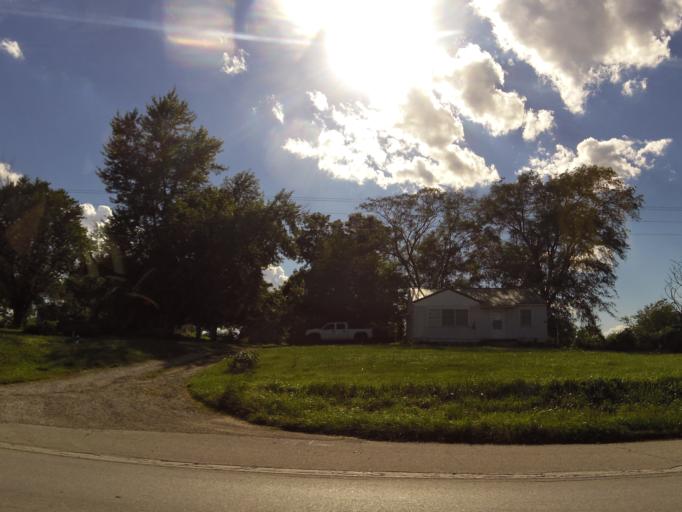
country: US
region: Missouri
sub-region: Marion County
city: Palmyra
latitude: 39.8692
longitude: -91.5255
